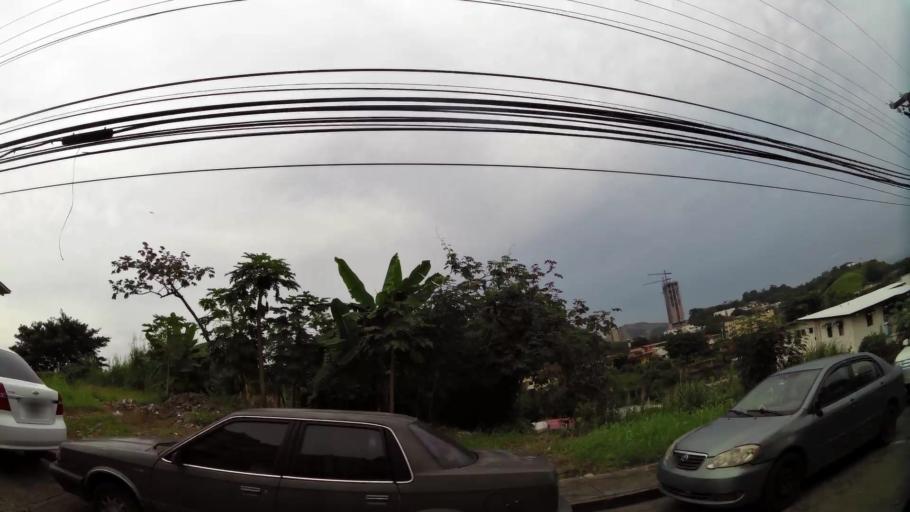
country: PA
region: Panama
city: Panama
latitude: 9.0194
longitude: -79.5192
